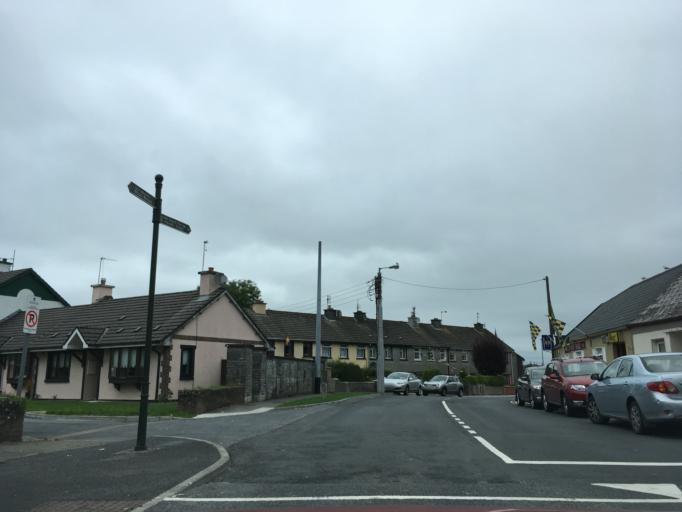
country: IE
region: Munster
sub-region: An Clar
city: Ennis
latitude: 52.8371
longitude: -8.9860
